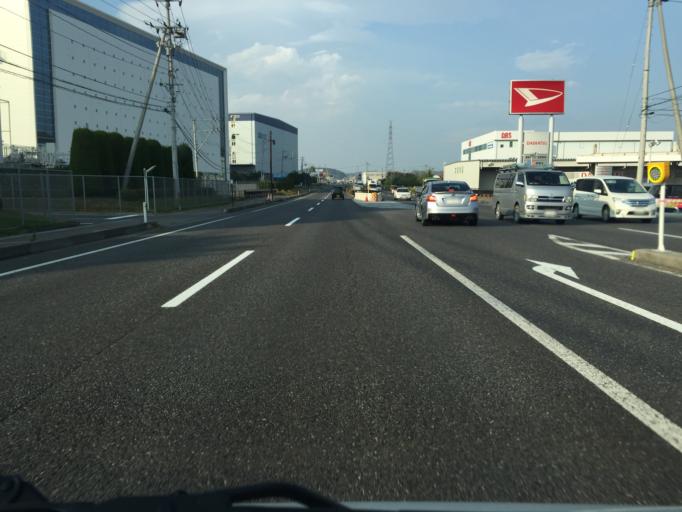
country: JP
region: Fukushima
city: Motomiya
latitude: 37.5250
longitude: 140.3959
